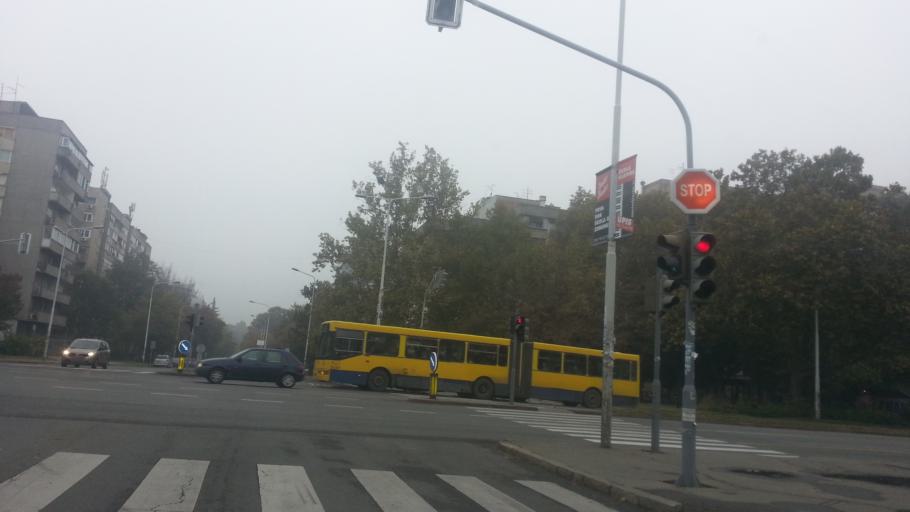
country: RS
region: Central Serbia
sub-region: Belgrade
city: Zemun
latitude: 44.8335
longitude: 20.4104
